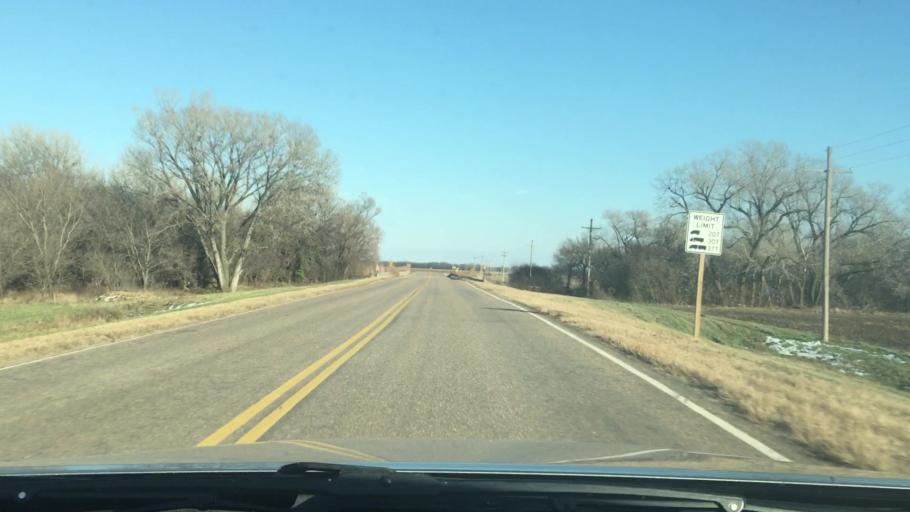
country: US
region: Kansas
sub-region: Rice County
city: Lyons
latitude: 38.2892
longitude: -98.1458
